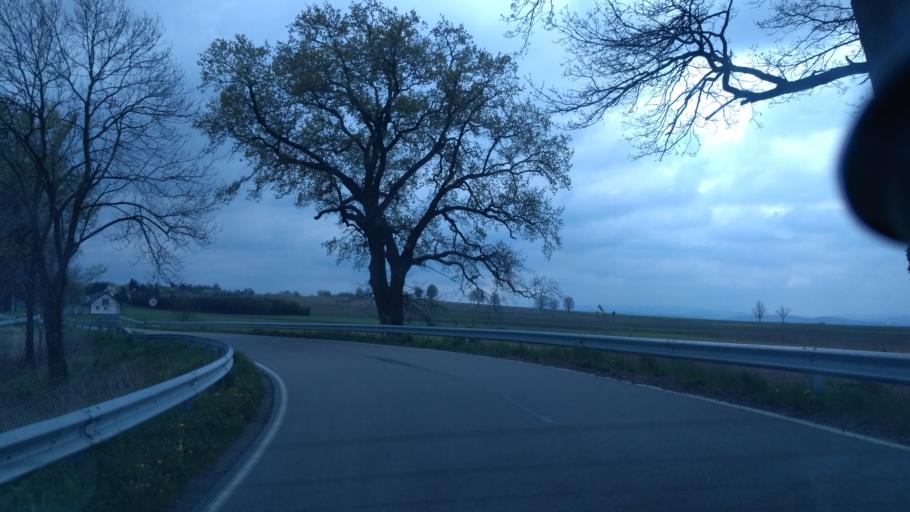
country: PL
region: Subcarpathian Voivodeship
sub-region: Powiat brzozowski
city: Jasionow
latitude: 49.6496
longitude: 21.9921
